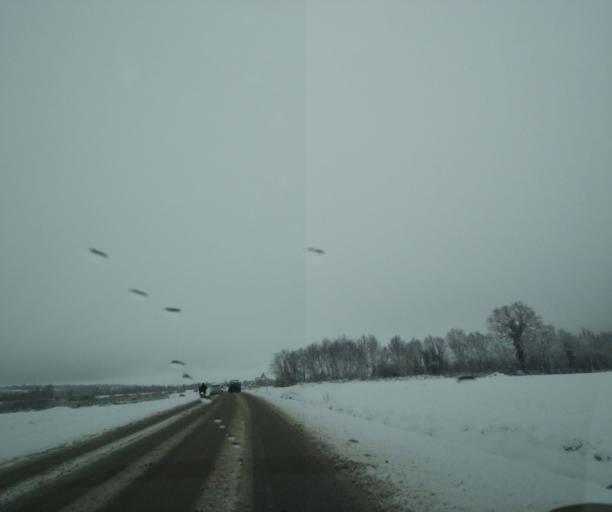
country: FR
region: Champagne-Ardenne
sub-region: Departement de la Haute-Marne
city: Wassy
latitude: 48.5389
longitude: 4.9244
